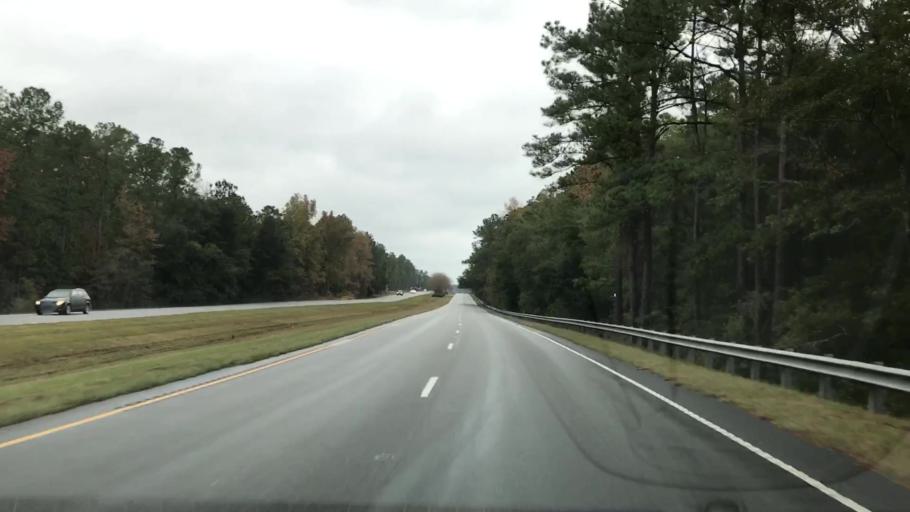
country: US
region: South Carolina
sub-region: Georgetown County
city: Georgetown
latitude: 33.2135
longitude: -79.3809
